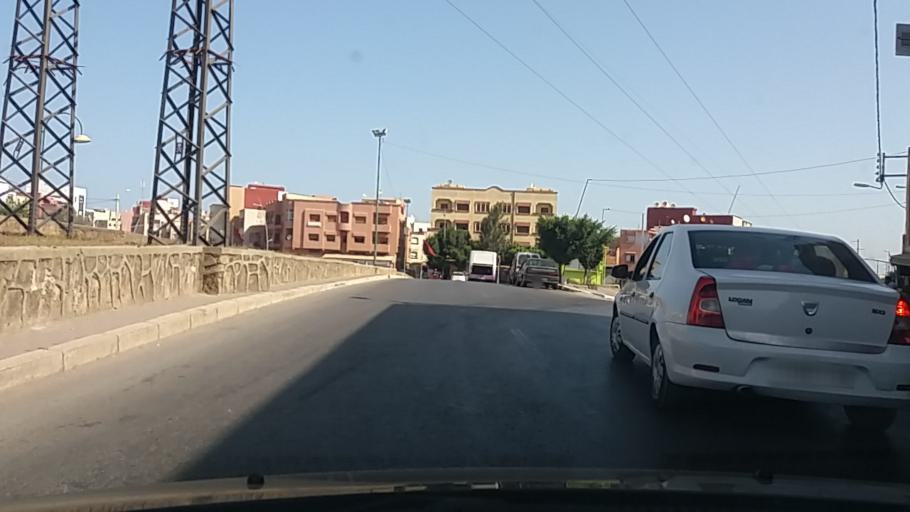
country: MA
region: Gharb-Chrarda-Beni Hssen
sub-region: Kenitra Province
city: Kenitra
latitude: 34.2649
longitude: -6.6169
